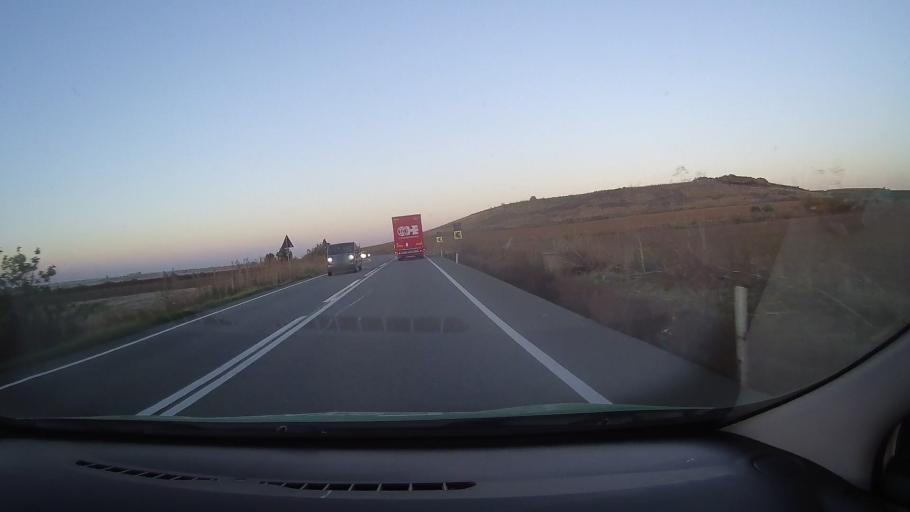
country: RO
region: Bihor
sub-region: Comuna Cherechiu
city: Cherechiu
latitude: 47.4013
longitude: 22.1647
